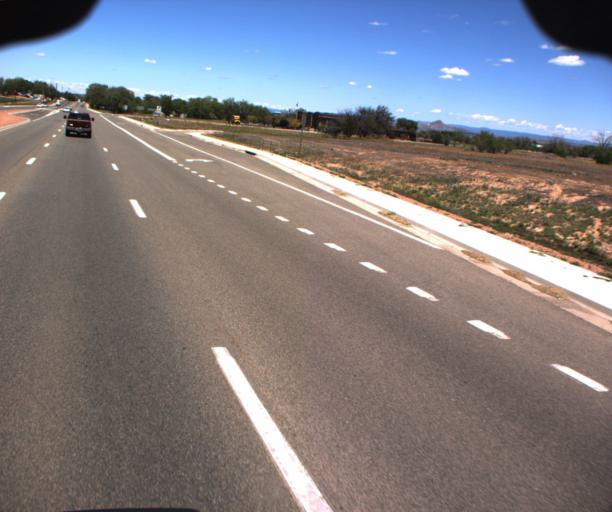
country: US
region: Arizona
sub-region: Yavapai County
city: Chino Valley
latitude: 34.7390
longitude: -112.4542
